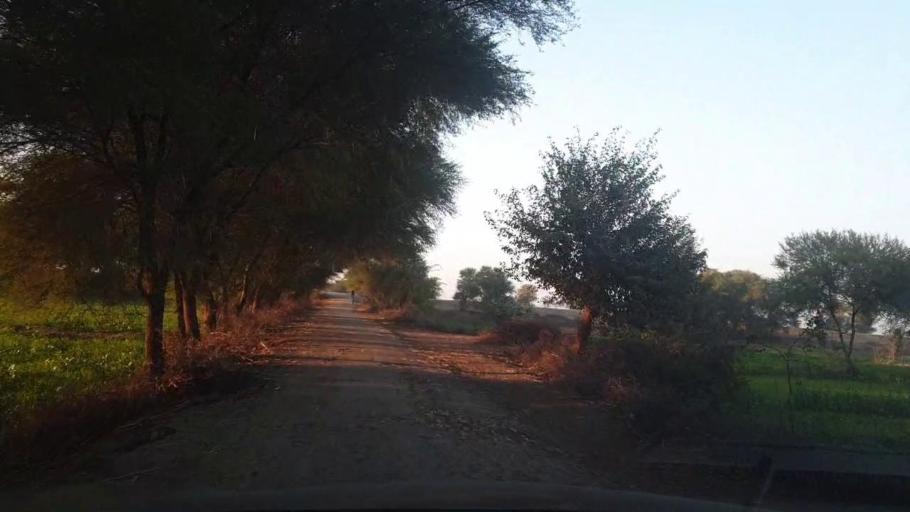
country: PK
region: Sindh
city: Ubauro
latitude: 28.1873
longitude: 69.6016
